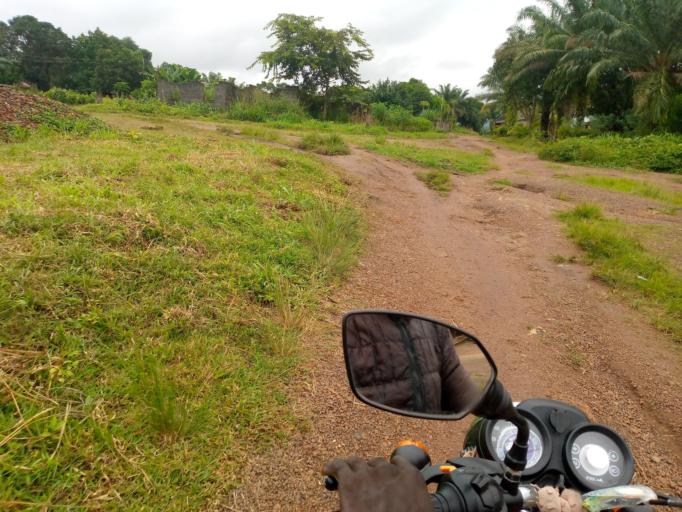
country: SL
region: Eastern Province
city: Kenema
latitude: 7.8467
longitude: -11.2025
